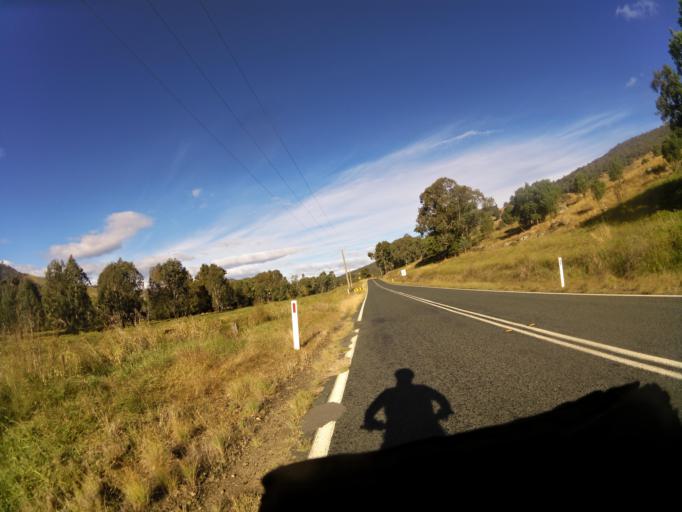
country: AU
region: New South Wales
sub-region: Greater Hume Shire
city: Holbrook
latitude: -35.9671
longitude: 147.7716
